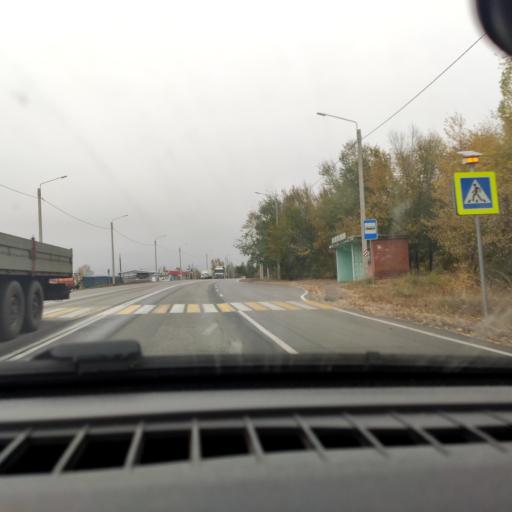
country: RU
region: Voronezj
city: Uryv-Pokrovka
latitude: 51.0435
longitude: 38.9819
